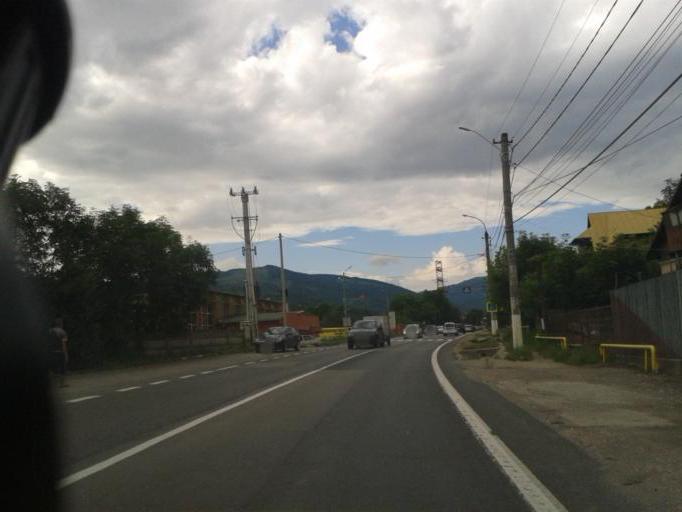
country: RO
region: Prahova
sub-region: Oras Breaza
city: Gura Beliei
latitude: 45.2271
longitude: 25.6391
